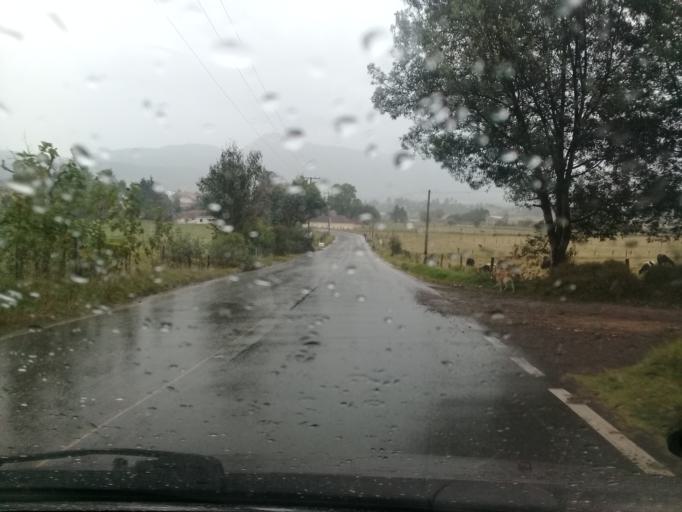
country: CO
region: Cundinamarca
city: Guasca
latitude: 4.8641
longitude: -73.8658
